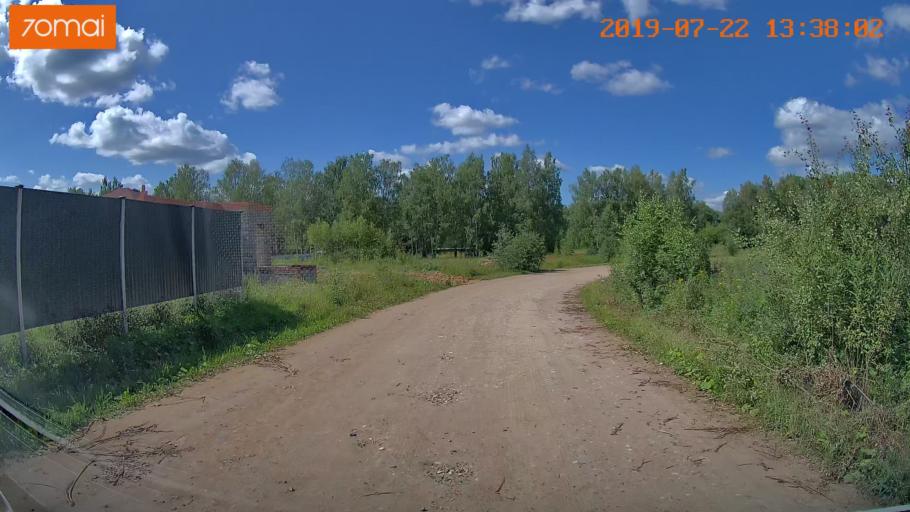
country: RU
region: Ivanovo
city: Novo-Talitsy
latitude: 57.0689
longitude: 40.8833
